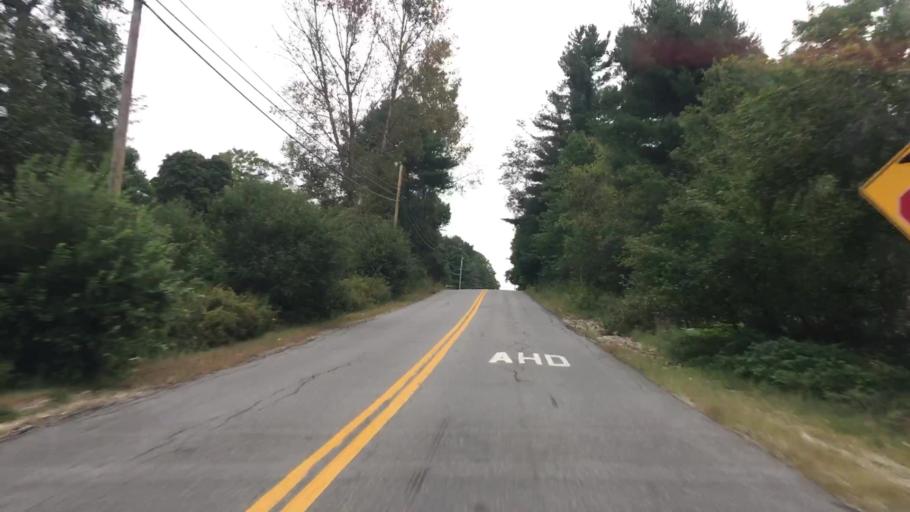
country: US
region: Maine
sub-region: Cumberland County
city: Freeport
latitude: 43.8933
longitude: -70.1866
